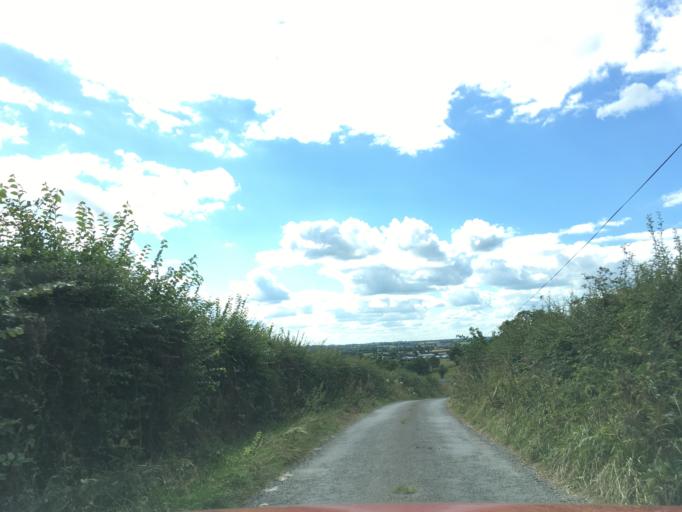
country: IE
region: Munster
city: Cashel
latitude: 52.4920
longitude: -7.9421
